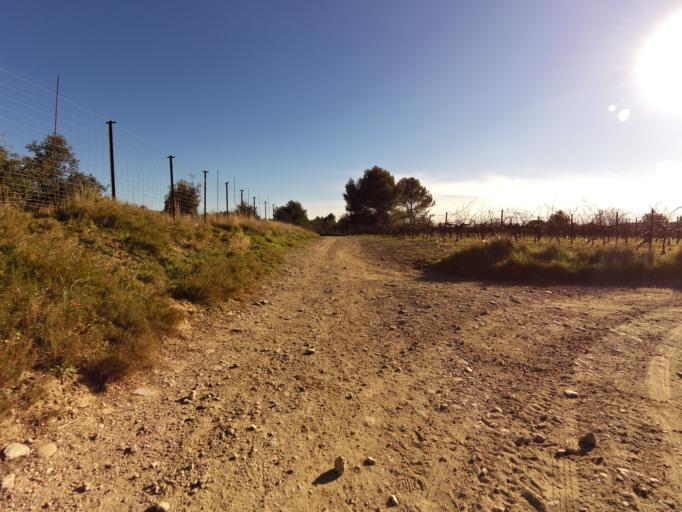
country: FR
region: Languedoc-Roussillon
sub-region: Departement du Gard
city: Gallargues-le-Montueux
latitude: 43.7318
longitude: 4.1620
